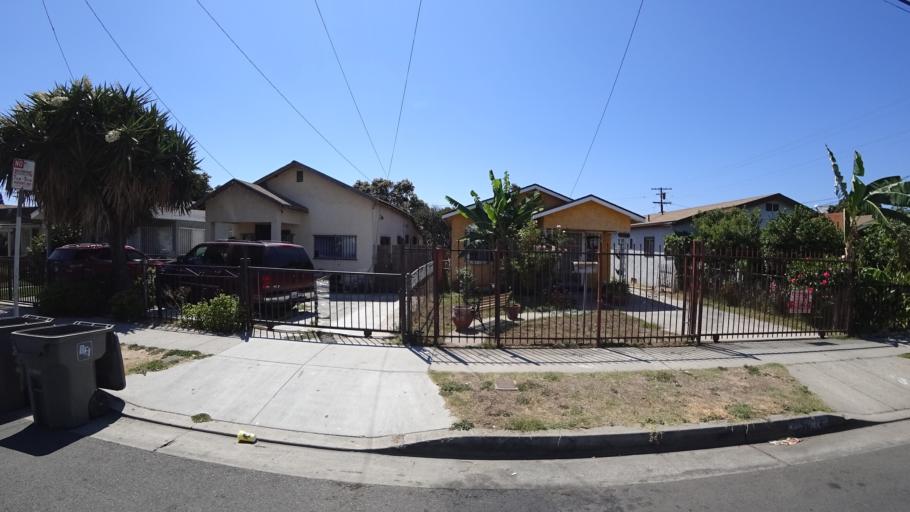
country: US
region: California
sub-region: Los Angeles County
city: Lennox
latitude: 33.9407
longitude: -118.3483
